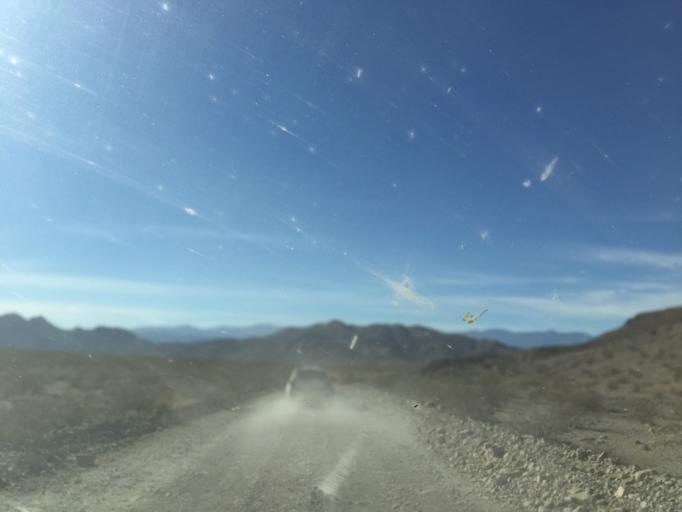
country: US
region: California
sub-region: Inyo County
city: Lone Pine
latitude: 36.7615
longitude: -117.5400
